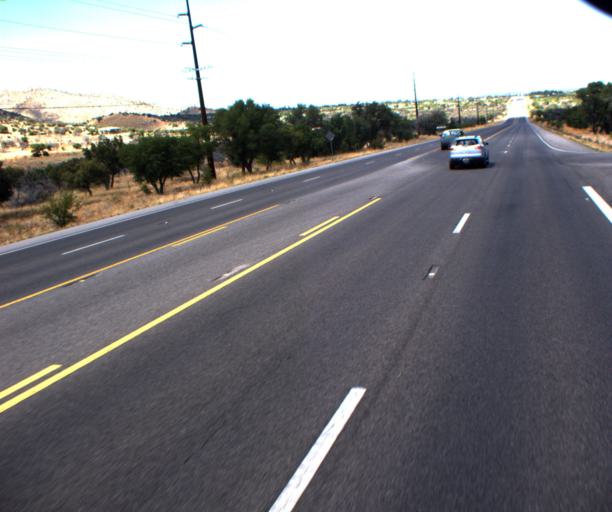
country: US
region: Arizona
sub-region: Cochise County
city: Sierra Vista Southeast
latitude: 31.4087
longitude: -110.2407
